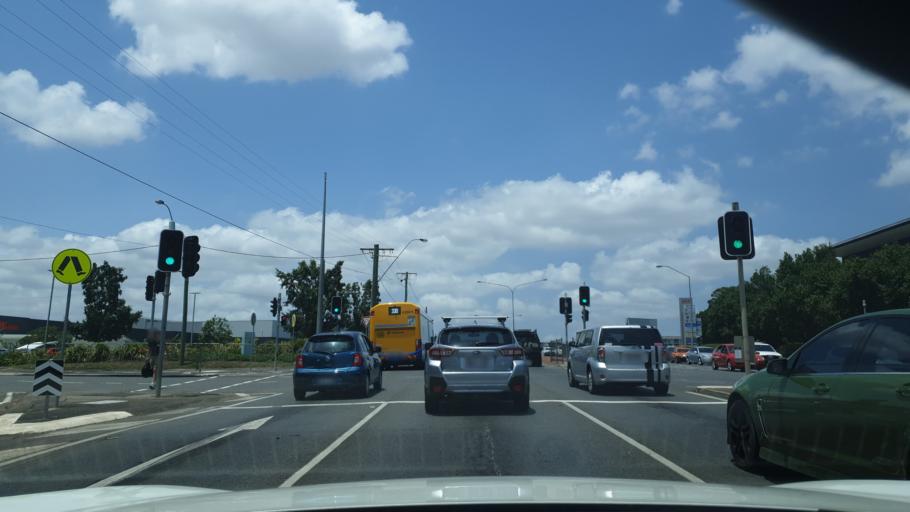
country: AU
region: Queensland
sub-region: Brisbane
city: Chermside West
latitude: -27.3815
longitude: 153.0299
